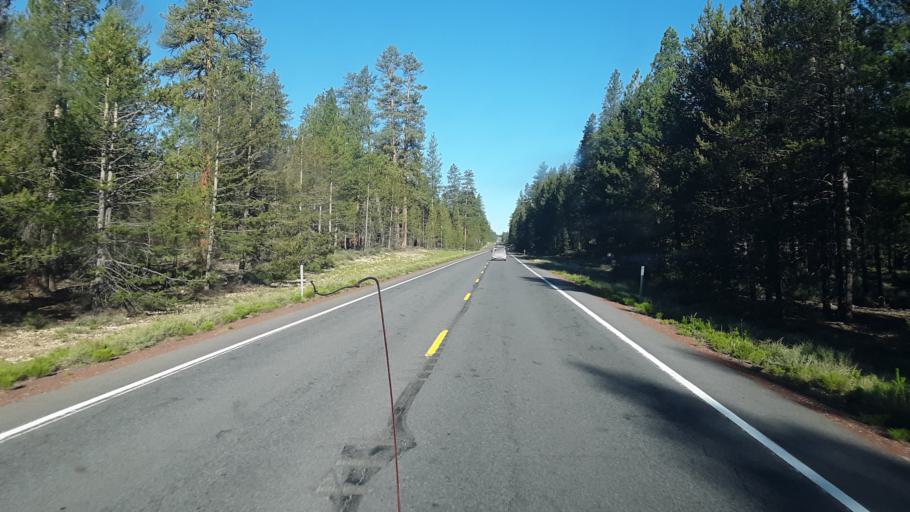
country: US
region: Oregon
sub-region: Deschutes County
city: La Pine
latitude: 43.0866
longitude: -121.9690
